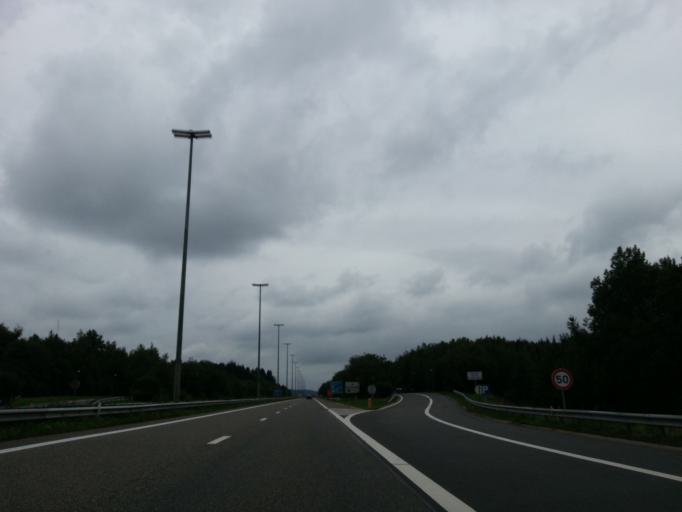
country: BE
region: Wallonia
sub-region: Province de Liege
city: Saint-Vith
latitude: 50.3154
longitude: 6.0842
